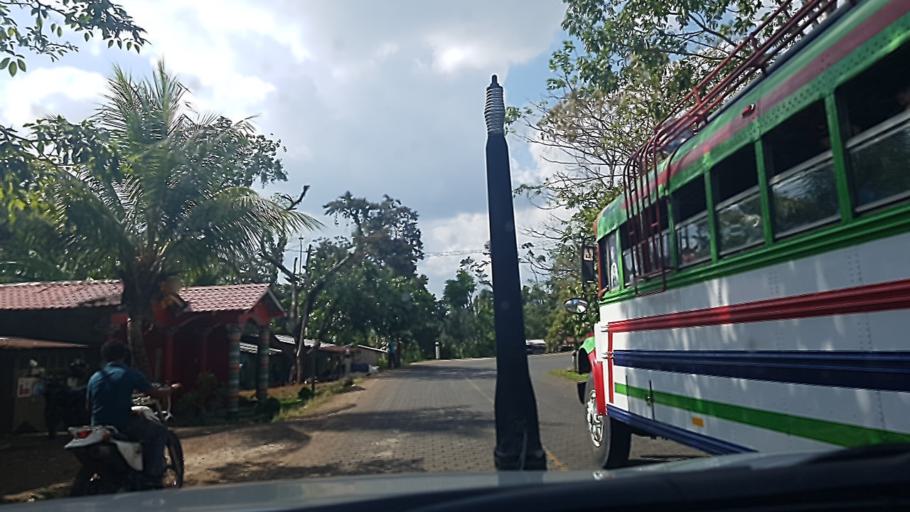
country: NI
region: Atlantico Sur
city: Nueva Guinea
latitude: 11.7048
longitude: -84.3723
